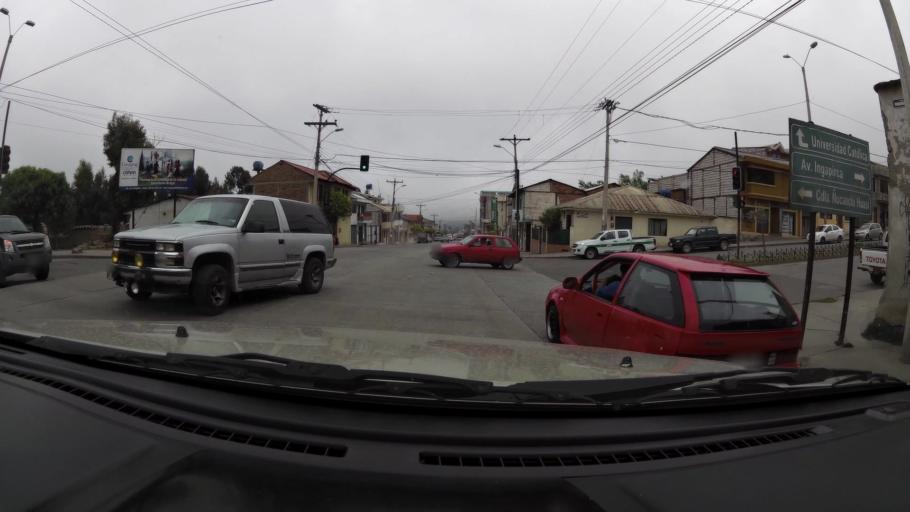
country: EC
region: Canar
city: Canar
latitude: -2.5531
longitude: -78.9417
